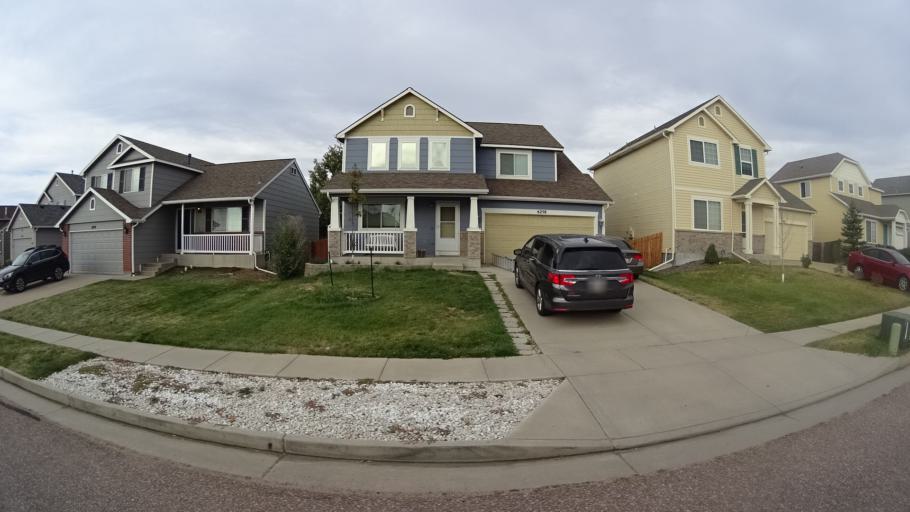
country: US
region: Colorado
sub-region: El Paso County
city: Cimarron Hills
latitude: 38.9229
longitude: -104.7104
